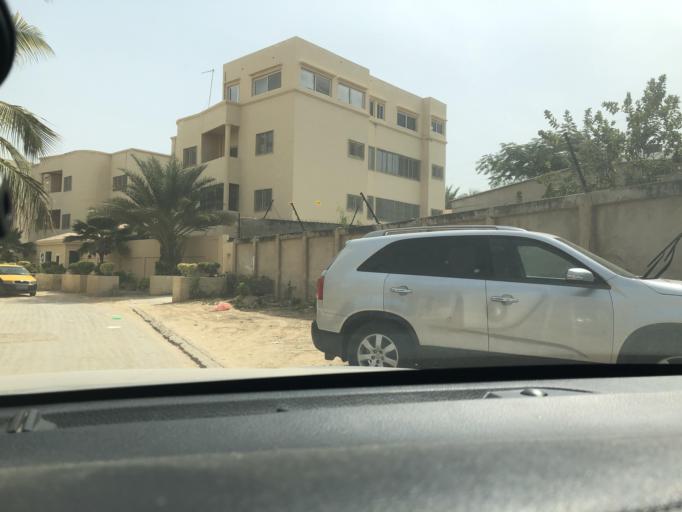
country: SN
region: Dakar
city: Mermoz Boabab
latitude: 14.7447
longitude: -17.5159
